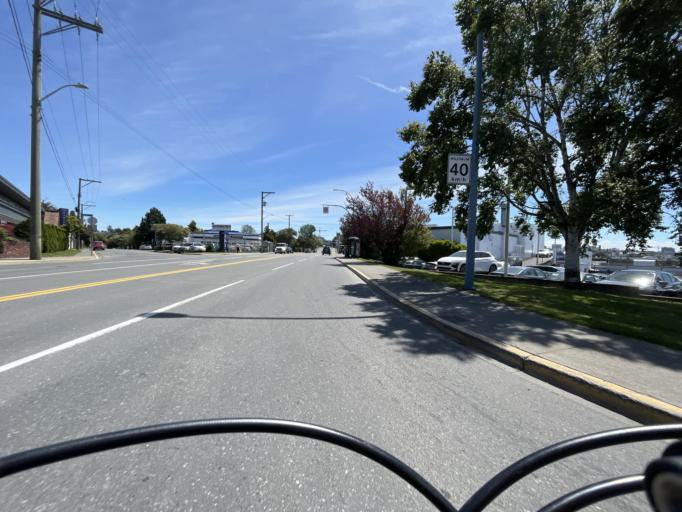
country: CA
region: British Columbia
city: Victoria
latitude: 48.4405
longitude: -123.3732
